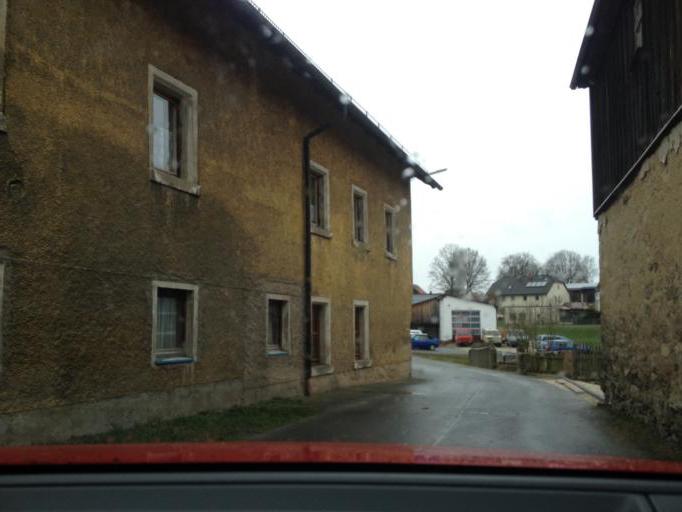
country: DE
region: Bavaria
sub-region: Upper Franconia
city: Thiersheim
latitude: 50.0869
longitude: 12.1357
